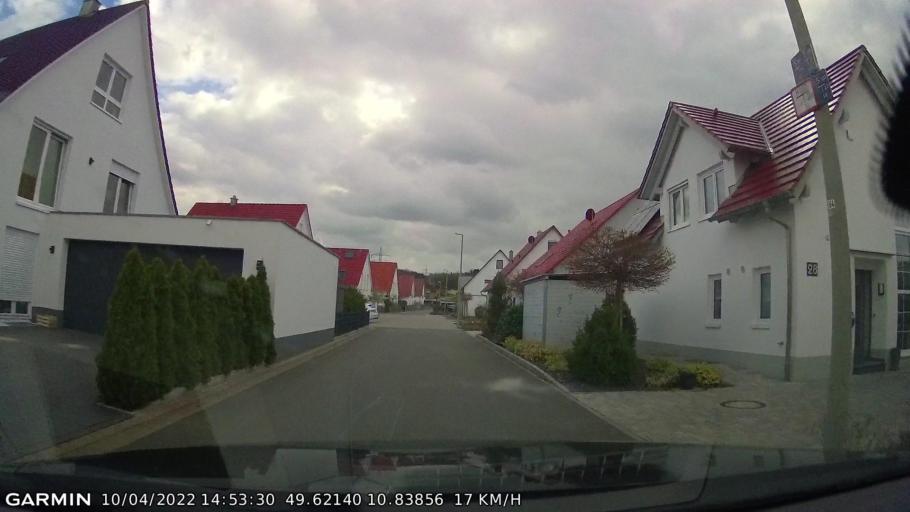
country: DE
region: Bavaria
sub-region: Regierungsbezirk Mittelfranken
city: Weisendorf
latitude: 49.6214
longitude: 10.8386
